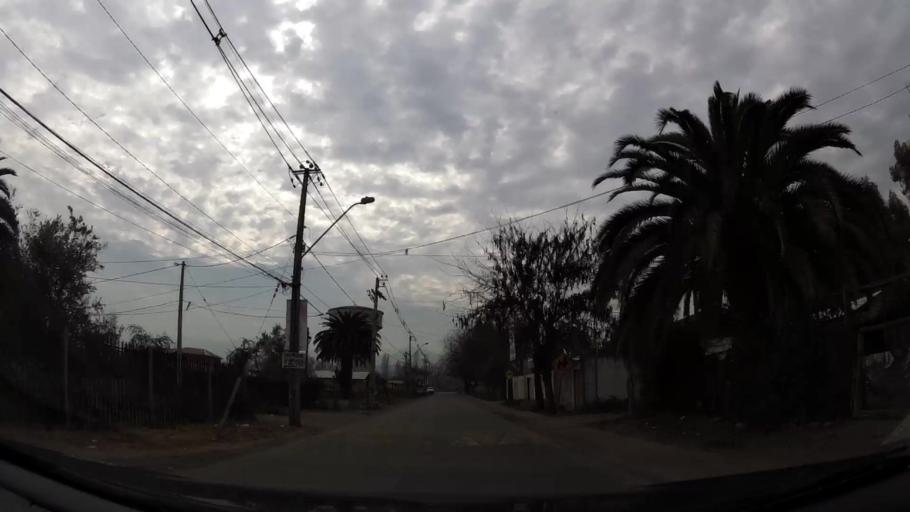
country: CL
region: Santiago Metropolitan
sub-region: Provincia de Chacabuco
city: Lampa
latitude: -33.2247
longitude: -70.7730
